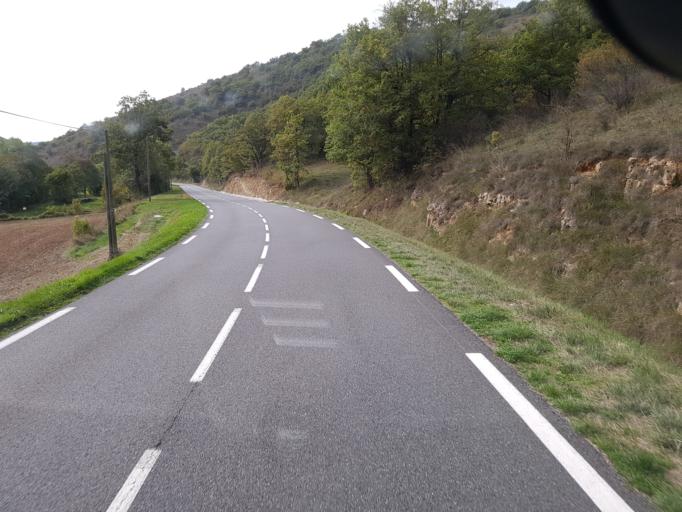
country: FR
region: Midi-Pyrenees
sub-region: Departement de l'Aveyron
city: Saint-Affrique
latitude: 43.9795
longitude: 2.9190
